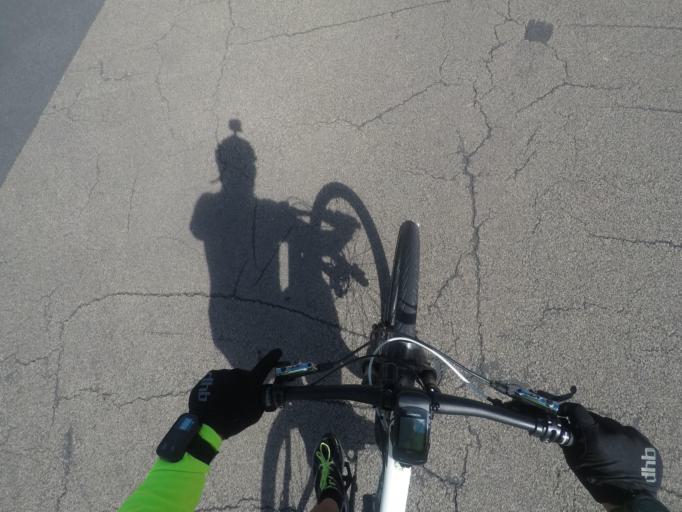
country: NZ
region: Auckland
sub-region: Auckland
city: Mangere
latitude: -36.9242
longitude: 174.7649
